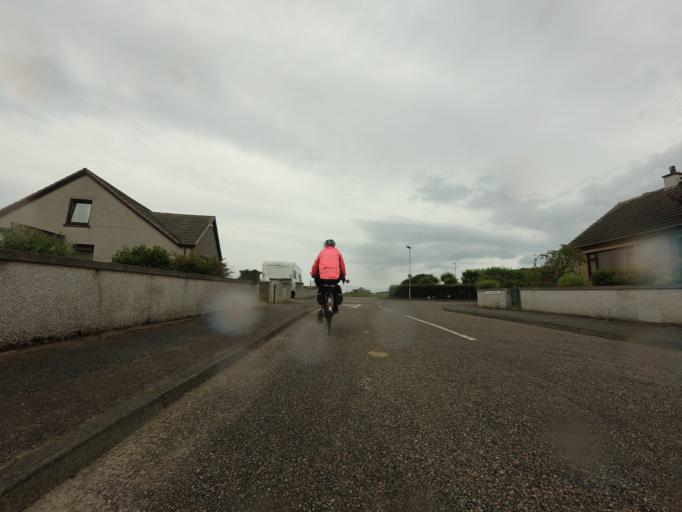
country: GB
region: Scotland
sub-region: Moray
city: Cullen
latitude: 57.6860
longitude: -2.8178
